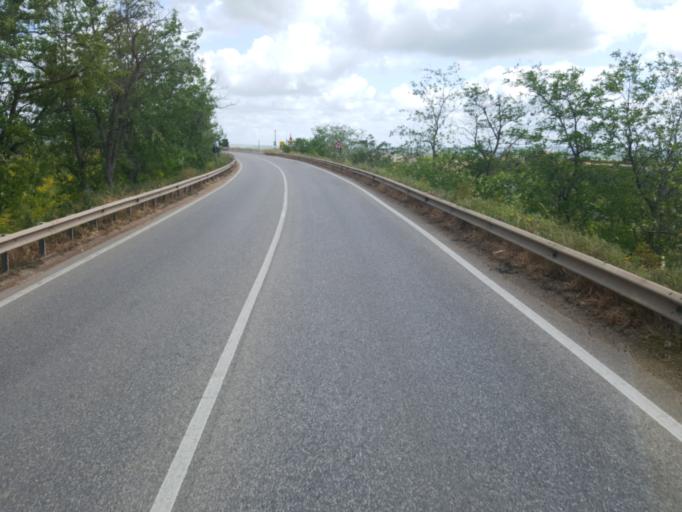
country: IT
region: Apulia
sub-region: Provincia di Bari
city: Altamura
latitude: 40.8143
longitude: 16.5588
